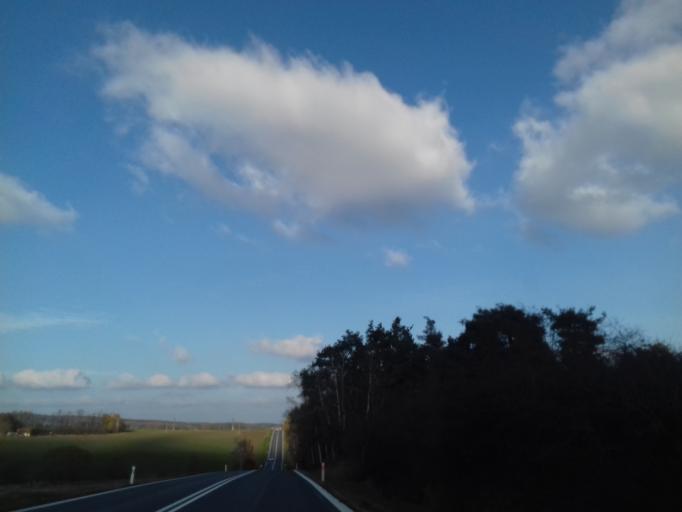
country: CZ
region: Plzensky
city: Holysov
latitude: 49.5829
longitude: 13.0831
